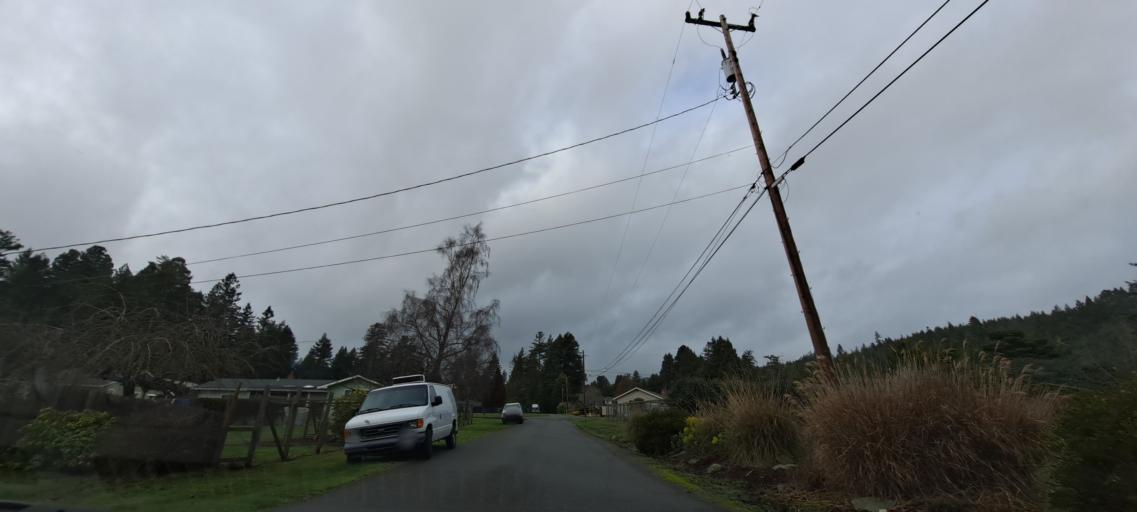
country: US
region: California
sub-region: Humboldt County
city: Fortuna
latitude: 40.6041
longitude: -124.1364
